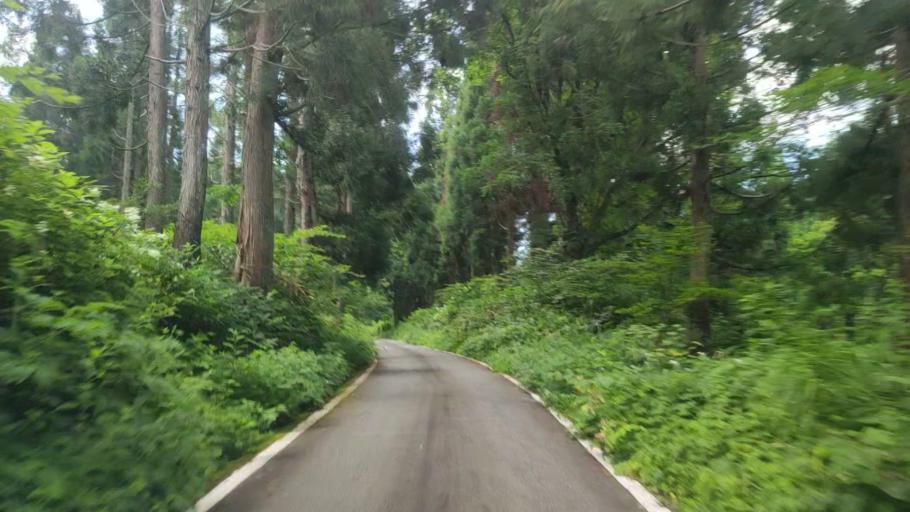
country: JP
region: Fukui
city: Katsuyama
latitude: 36.1713
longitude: 136.5240
